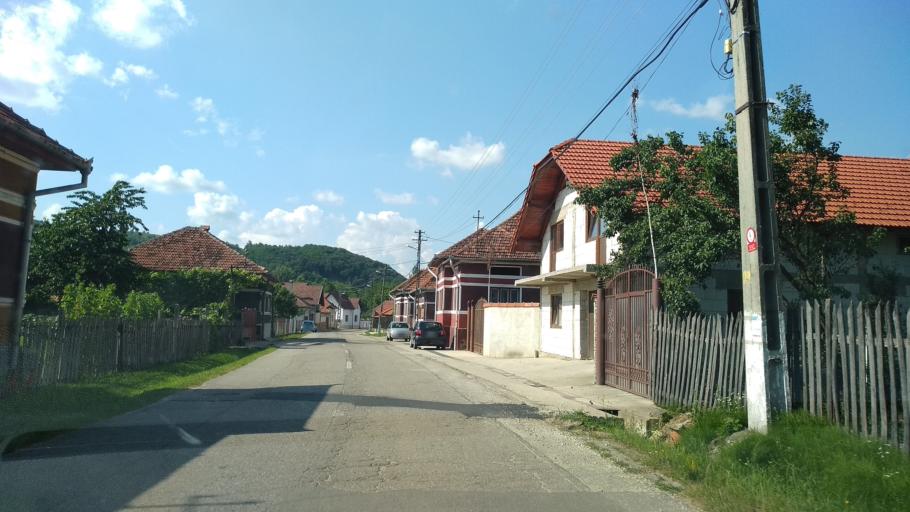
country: RO
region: Hunedoara
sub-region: Comuna Orastioara de Sus
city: Orastioara de Sus
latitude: 45.7049
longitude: 23.1651
